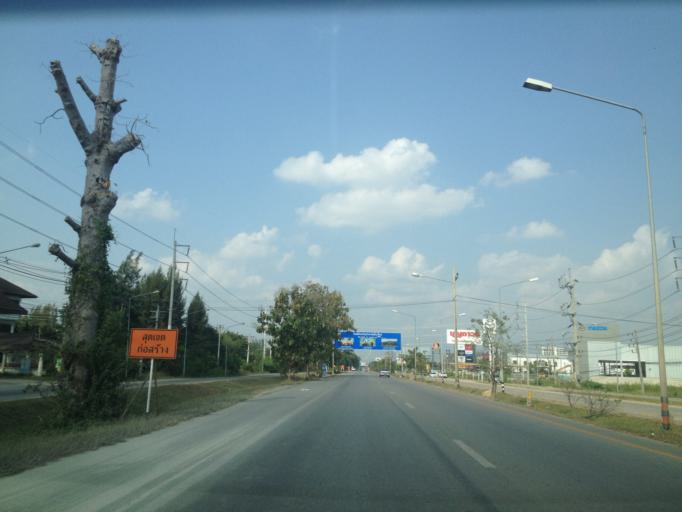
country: TH
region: Chiang Mai
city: Saraphi
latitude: 18.7404
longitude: 99.0359
